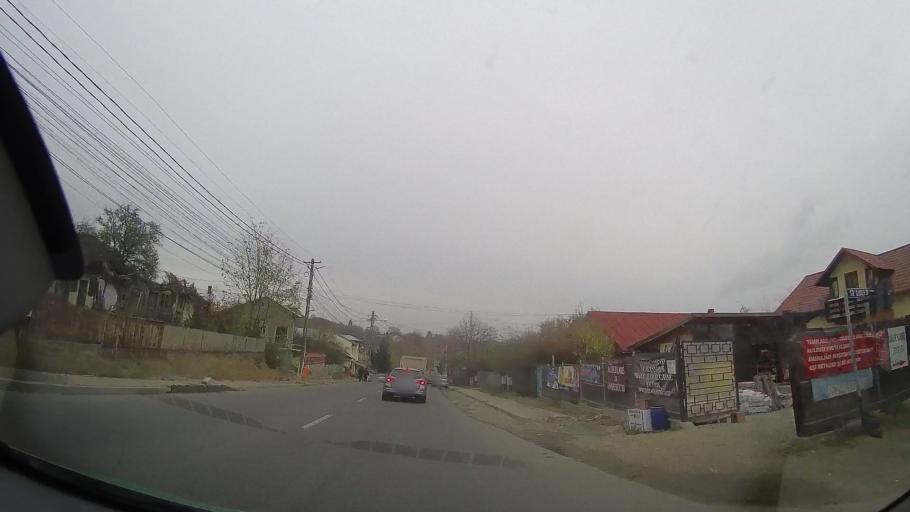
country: RO
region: Prahova
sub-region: Oras Baicoi
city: Tintea
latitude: 45.0343
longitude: 25.8989
